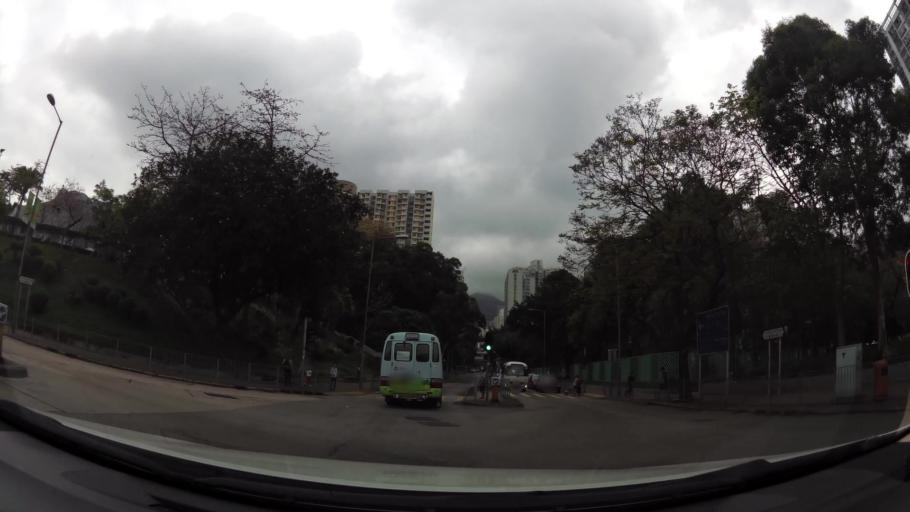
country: HK
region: Wong Tai Sin
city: Wong Tai Sin
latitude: 22.3368
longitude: 114.1918
